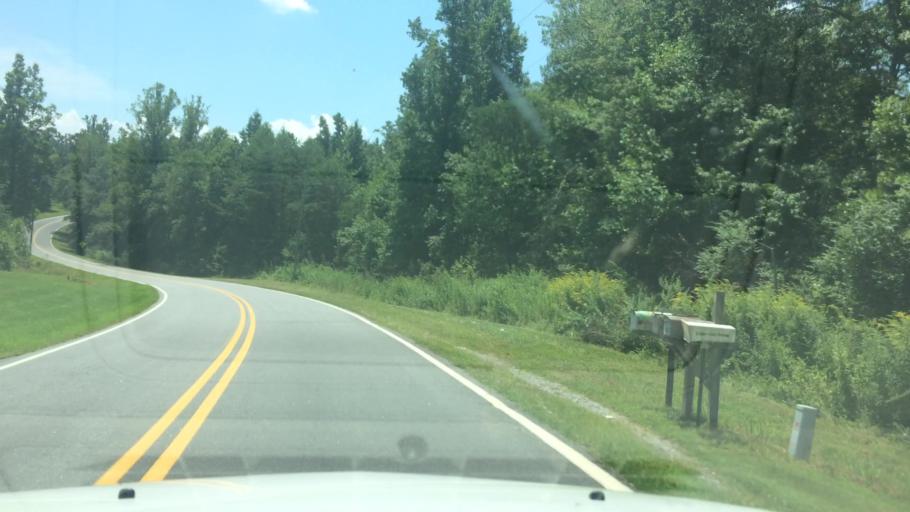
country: US
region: North Carolina
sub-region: Alexander County
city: Taylorsville
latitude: 35.9468
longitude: -81.2678
